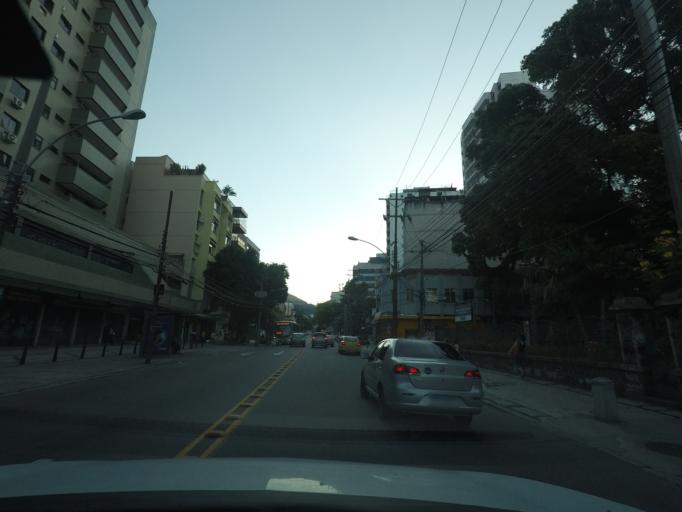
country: BR
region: Rio de Janeiro
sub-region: Rio De Janeiro
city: Rio de Janeiro
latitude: -22.9355
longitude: -43.2439
